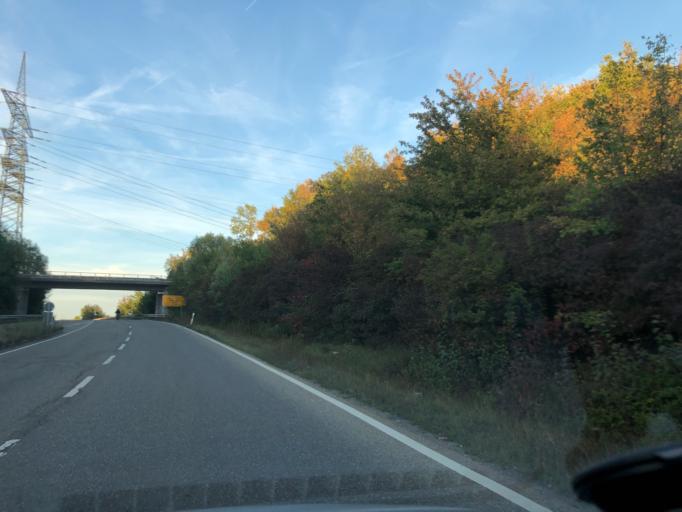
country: DE
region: Baden-Wuerttemberg
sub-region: Regierungsbezirk Stuttgart
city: Kornwestheim
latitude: 48.8439
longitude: 9.1798
